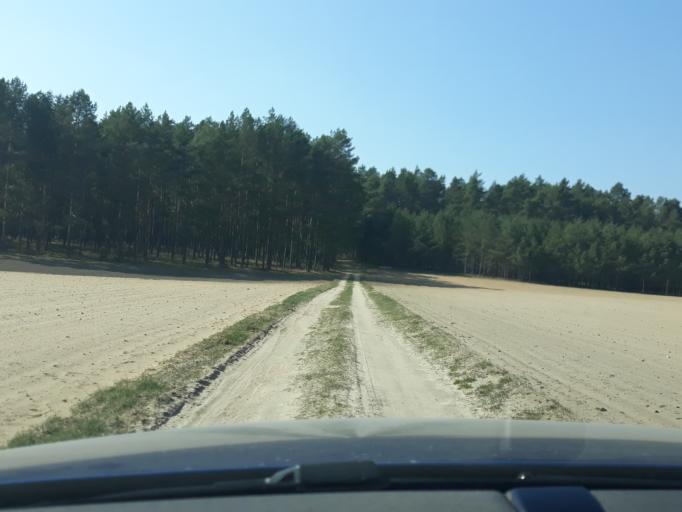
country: PL
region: Pomeranian Voivodeship
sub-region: Powiat bytowski
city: Lipnica
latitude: 53.8609
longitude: 17.4314
